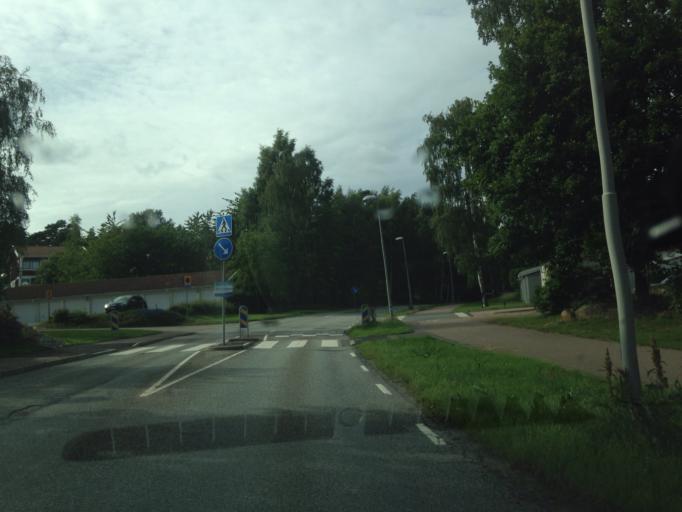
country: SE
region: Vaestra Goetaland
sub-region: Goteborg
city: Goeteborg
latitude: 57.7586
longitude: 11.9662
